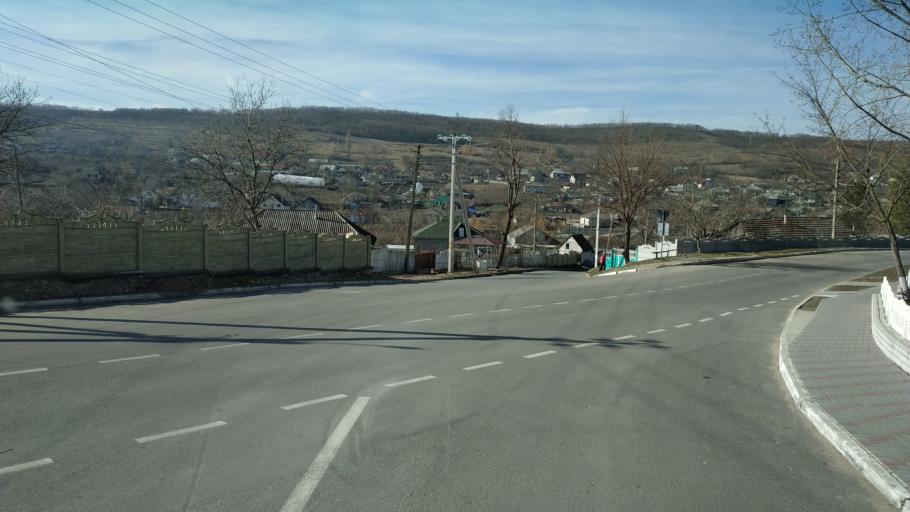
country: MD
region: Chisinau
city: Vatra
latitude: 47.0268
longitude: 28.6334
